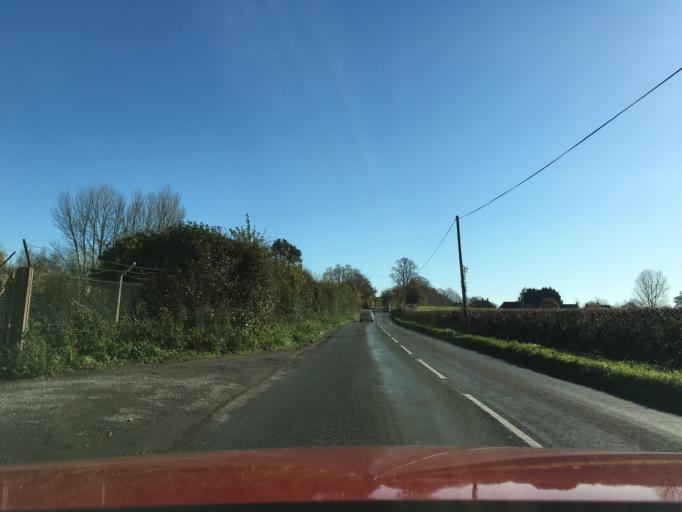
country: GB
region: England
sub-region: Somerset
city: Yeovil
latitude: 50.9583
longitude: -2.6557
